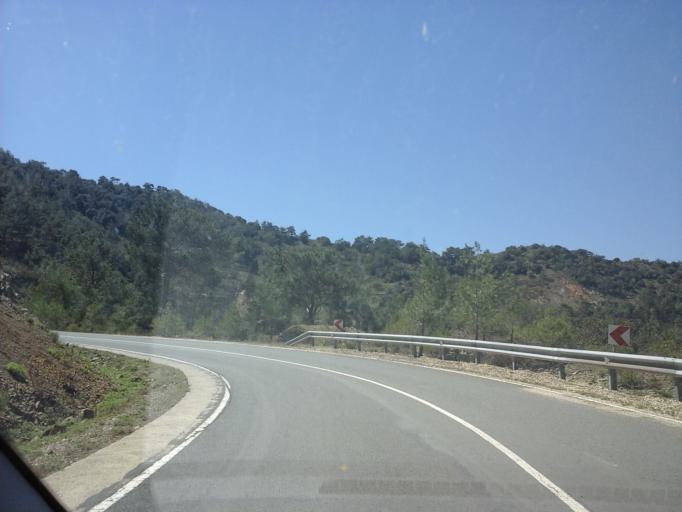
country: CY
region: Lefkosia
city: Kakopetria
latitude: 35.0019
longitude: 32.7972
